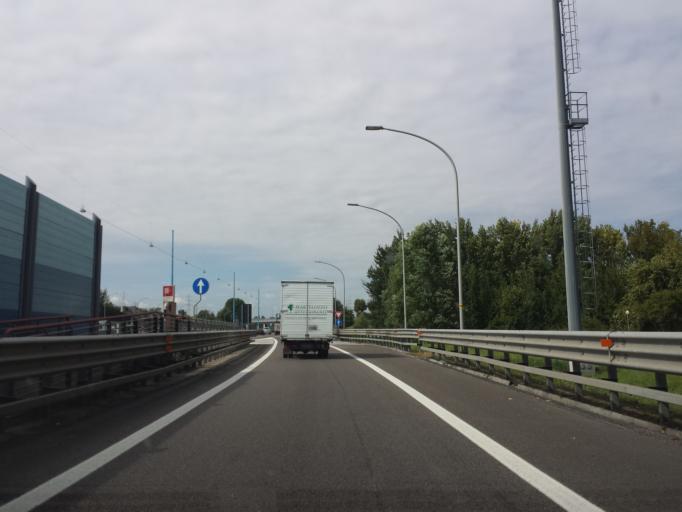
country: IT
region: Veneto
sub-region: Provincia di Venezia
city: Mestre
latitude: 45.4735
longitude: 12.2059
